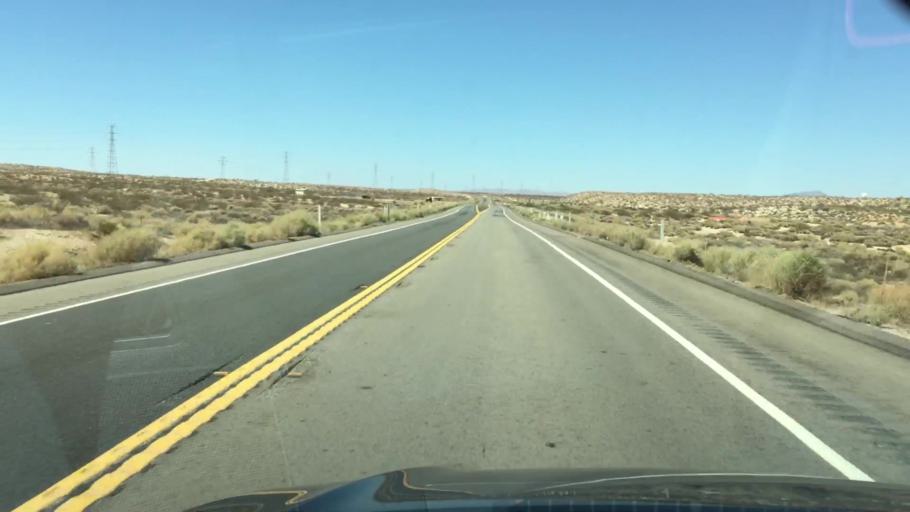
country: US
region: California
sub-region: Kern County
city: Boron
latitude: 35.0735
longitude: -117.5601
